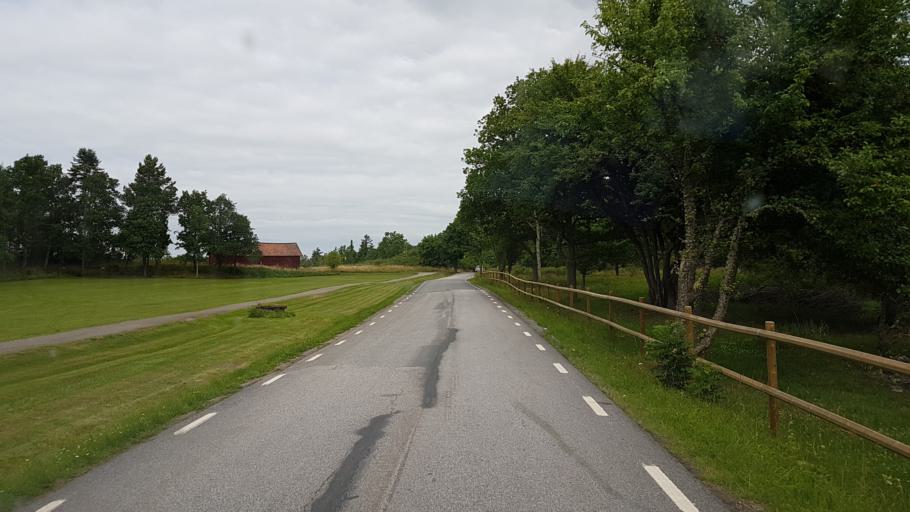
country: SE
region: OEstergoetland
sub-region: Valdemarsviks Kommun
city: Gusum
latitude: 58.4347
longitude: 16.5996
